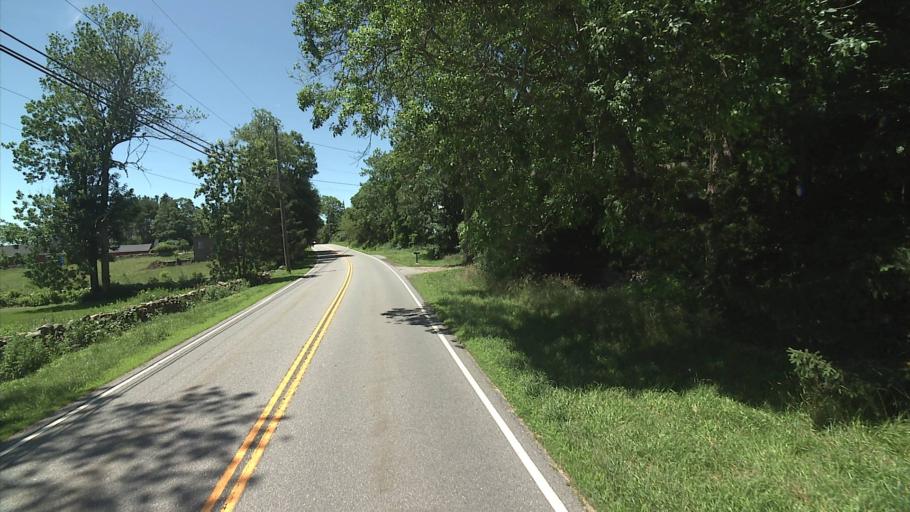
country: US
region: Connecticut
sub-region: New London County
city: Pawcatuck
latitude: 41.3821
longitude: -71.8864
